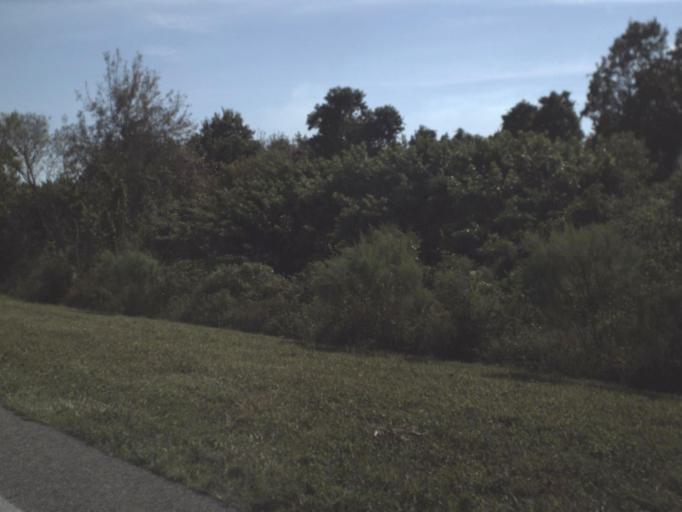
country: US
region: Florida
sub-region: Hendry County
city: Port LaBelle
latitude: 26.9719
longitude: -81.3175
